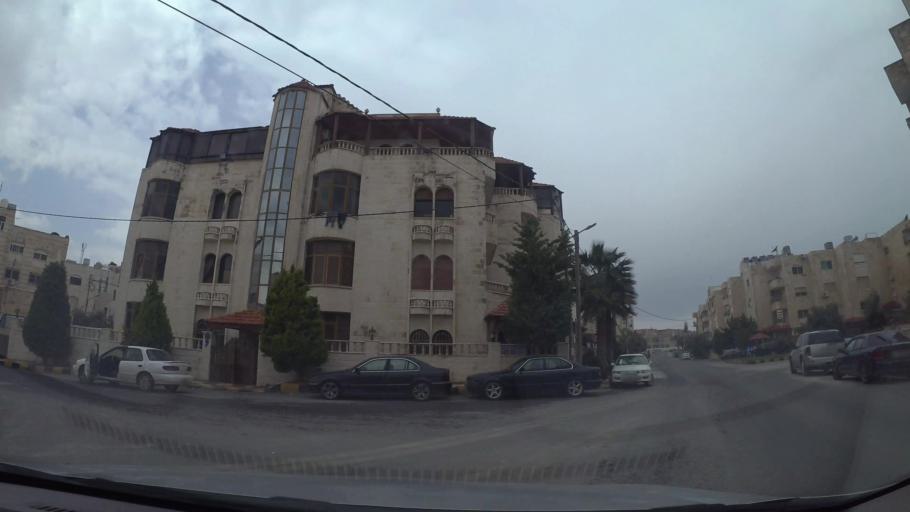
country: JO
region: Amman
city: Umm as Summaq
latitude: 31.8994
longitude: 35.8458
